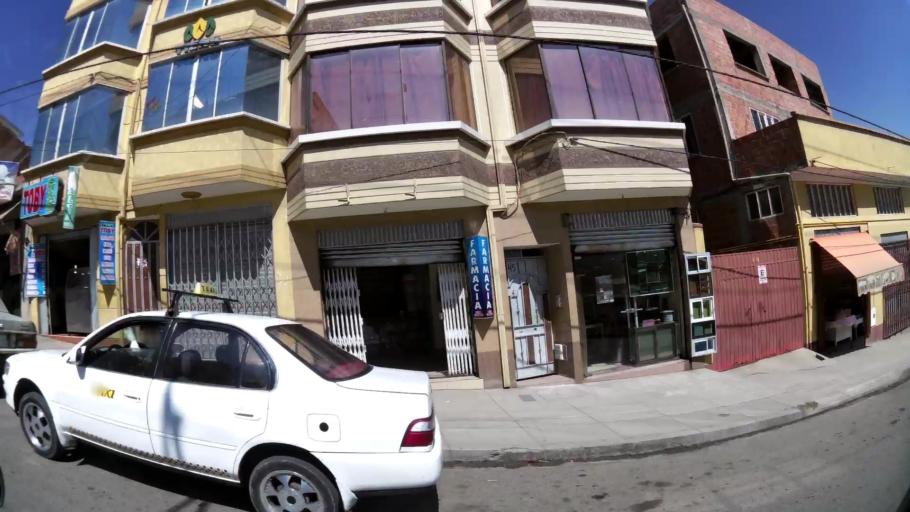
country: BO
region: La Paz
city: La Paz
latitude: -16.5341
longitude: -68.0385
